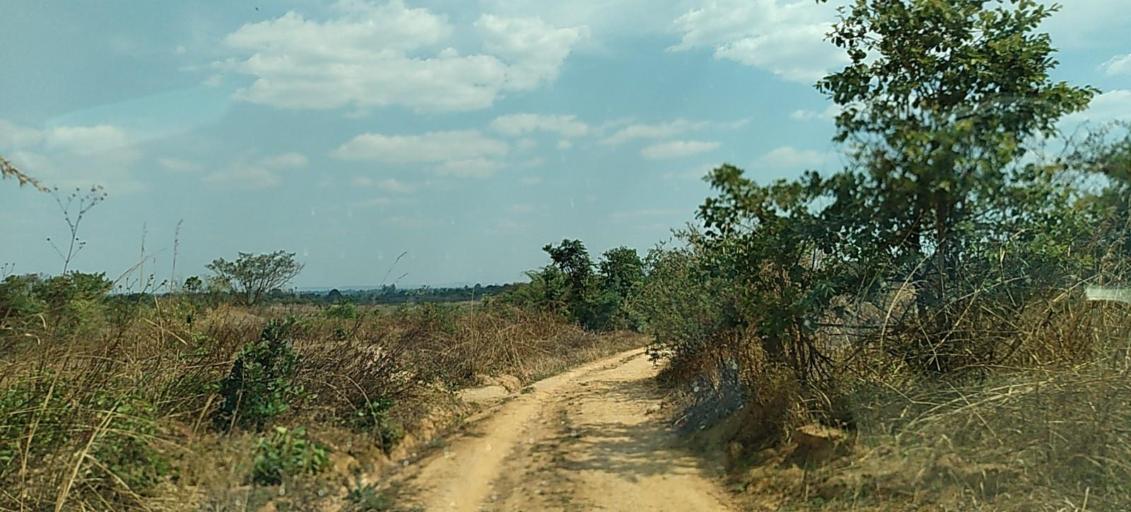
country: ZM
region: Copperbelt
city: Chililabombwe
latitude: -12.3252
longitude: 27.7882
